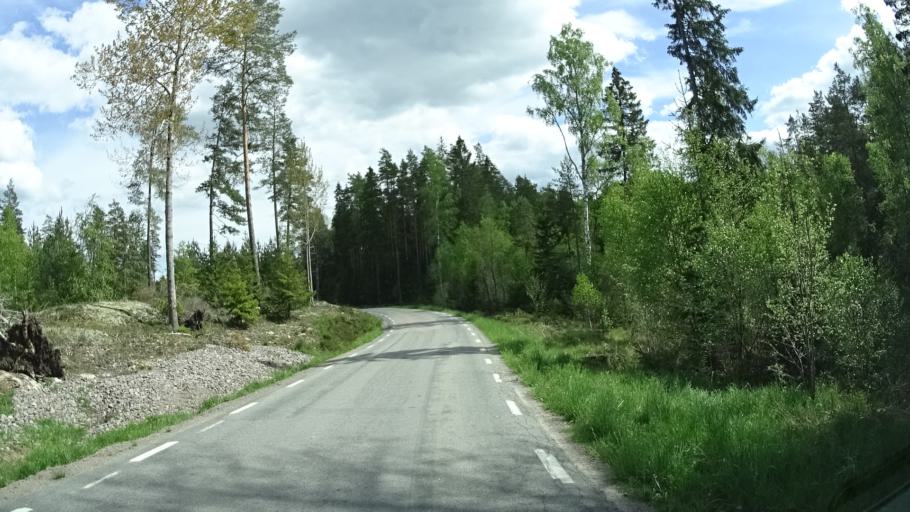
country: SE
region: OEstergoetland
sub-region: Finspangs Kommun
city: Finspang
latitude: 58.6102
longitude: 15.7295
